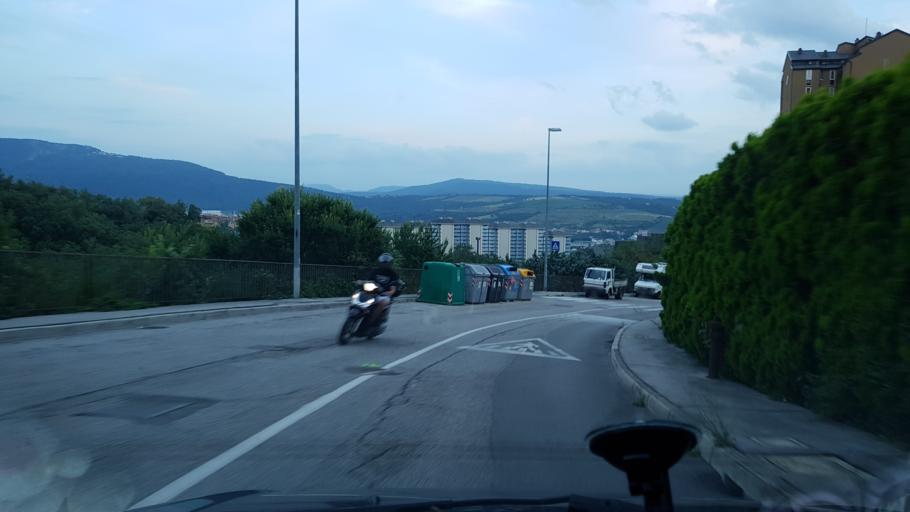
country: IT
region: Friuli Venezia Giulia
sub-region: Provincia di Trieste
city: Domio
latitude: 45.6278
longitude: 13.8215
